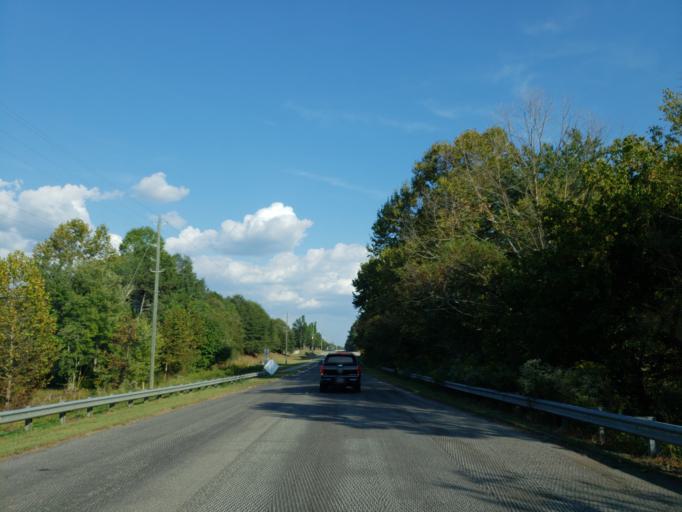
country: US
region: Georgia
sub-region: Cobb County
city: Powder Springs
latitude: 33.8686
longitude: -84.7068
